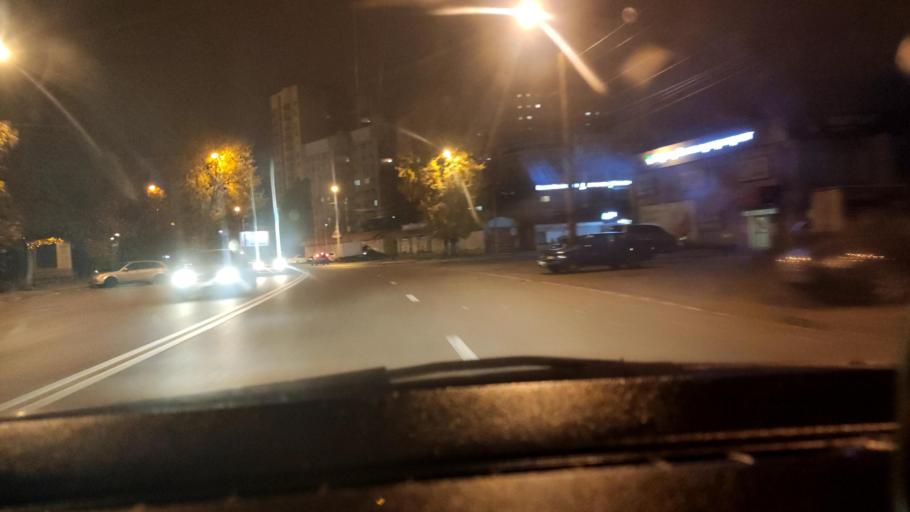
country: RU
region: Voronezj
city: Podgornoye
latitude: 51.7083
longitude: 39.1485
